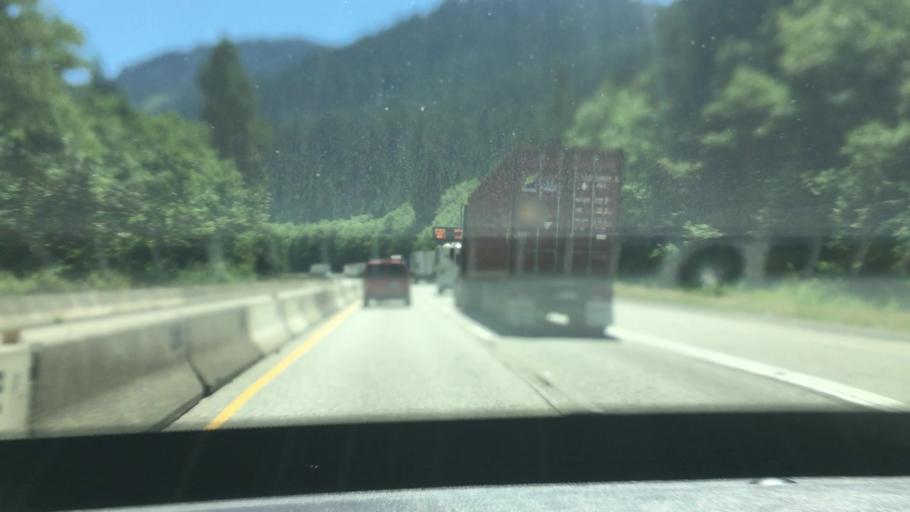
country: US
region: Washington
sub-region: King County
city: Tanner
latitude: 47.3940
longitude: -121.4748
